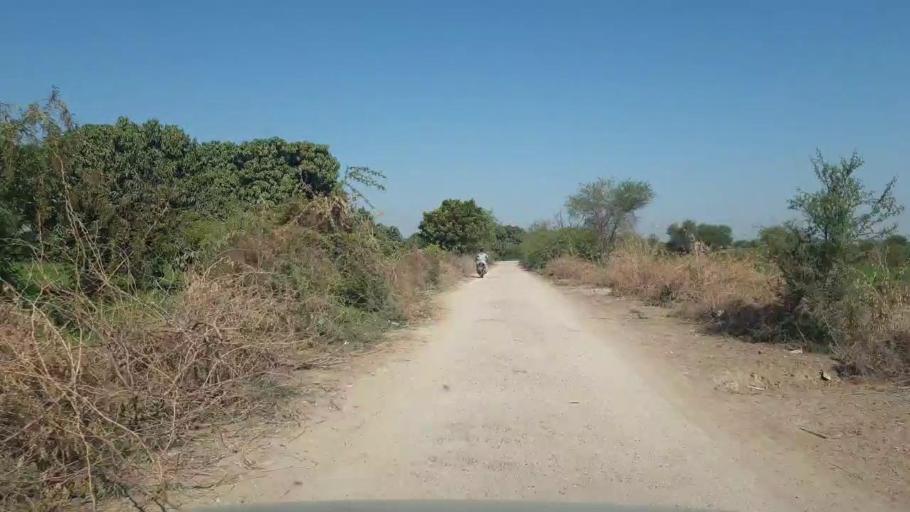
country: PK
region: Sindh
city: Mirwah Gorchani
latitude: 25.3117
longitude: 69.1042
